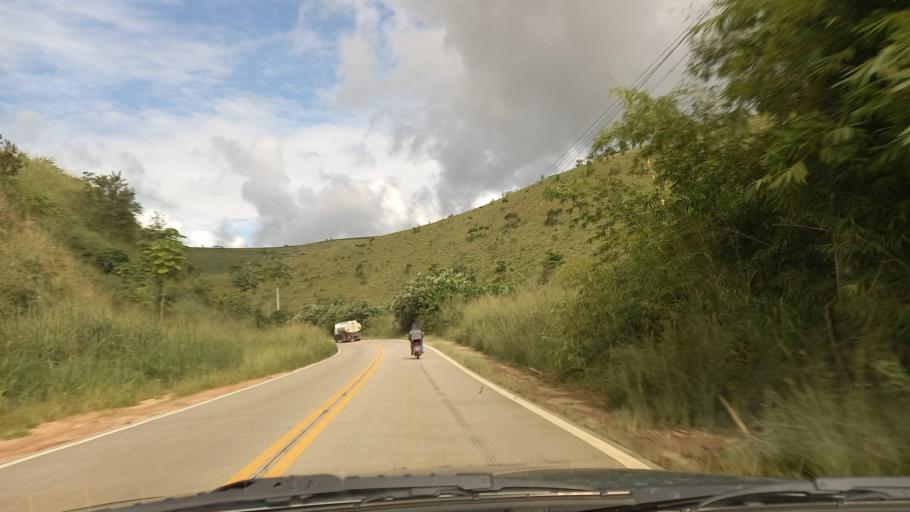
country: BR
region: Pernambuco
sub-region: Maraial
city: Maraial
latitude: -8.7492
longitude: -35.8309
